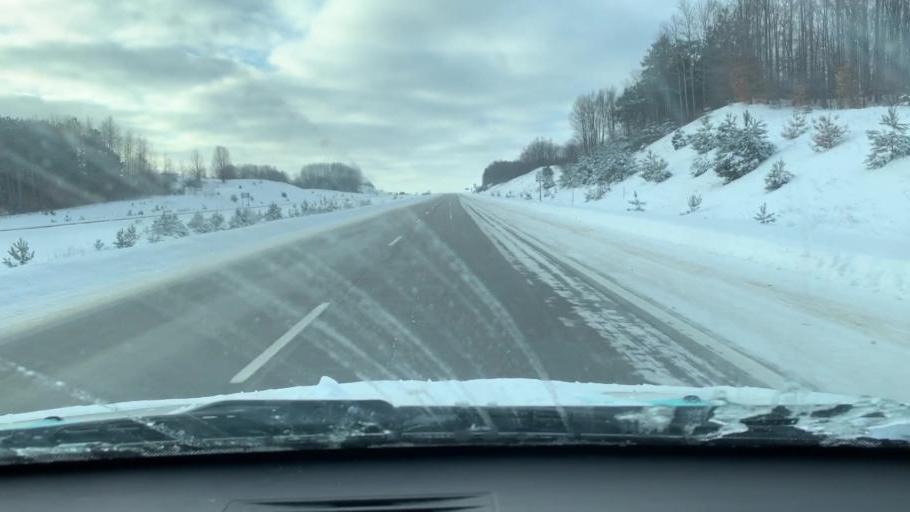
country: US
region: Michigan
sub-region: Wexford County
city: Manton
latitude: 44.3986
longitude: -85.3821
